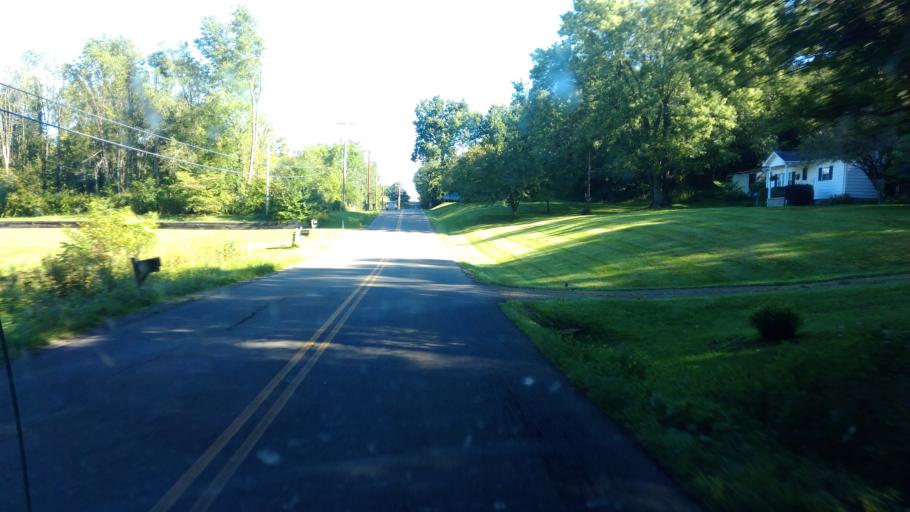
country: US
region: Ohio
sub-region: Knox County
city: Gambier
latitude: 40.4136
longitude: -82.3686
